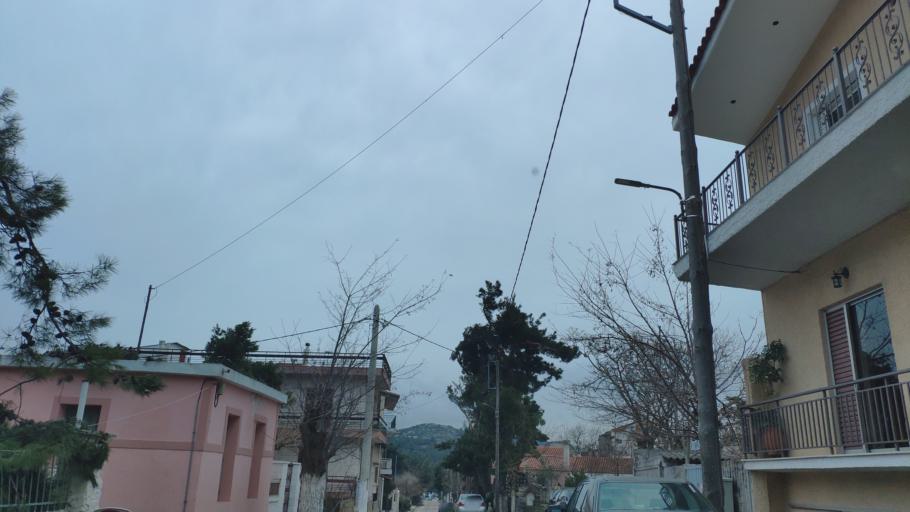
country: GR
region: Attica
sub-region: Nomarchia Dytikis Attikis
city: Vilia
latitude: 38.1668
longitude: 23.3382
